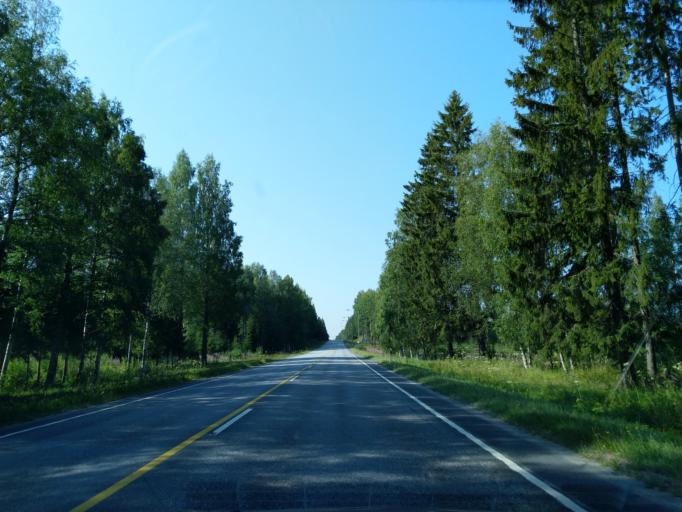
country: FI
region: Satakunta
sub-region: Pori
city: Pomarkku
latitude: 61.6530
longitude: 21.9604
